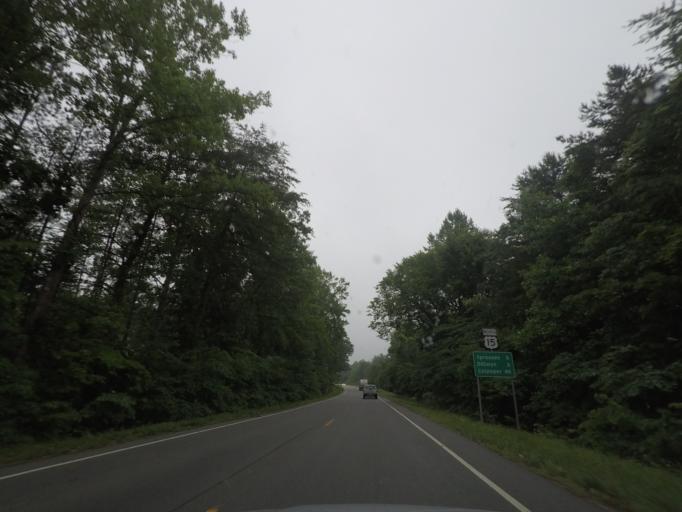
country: US
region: Virginia
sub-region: Buckingham County
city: Buckingham
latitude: 37.4502
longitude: -78.4576
